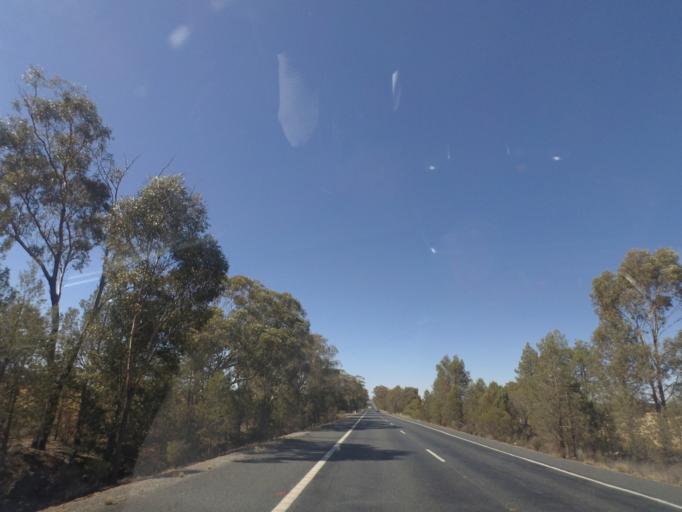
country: AU
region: New South Wales
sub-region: Bland
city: West Wyalong
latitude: -34.1706
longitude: 147.1151
